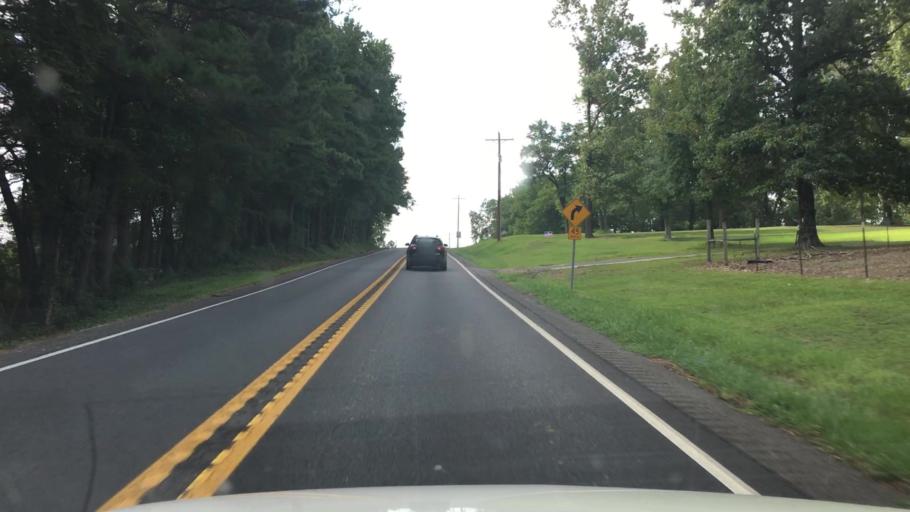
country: US
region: Arkansas
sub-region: Garland County
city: Lake Hamilton
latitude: 34.3277
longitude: -93.1739
